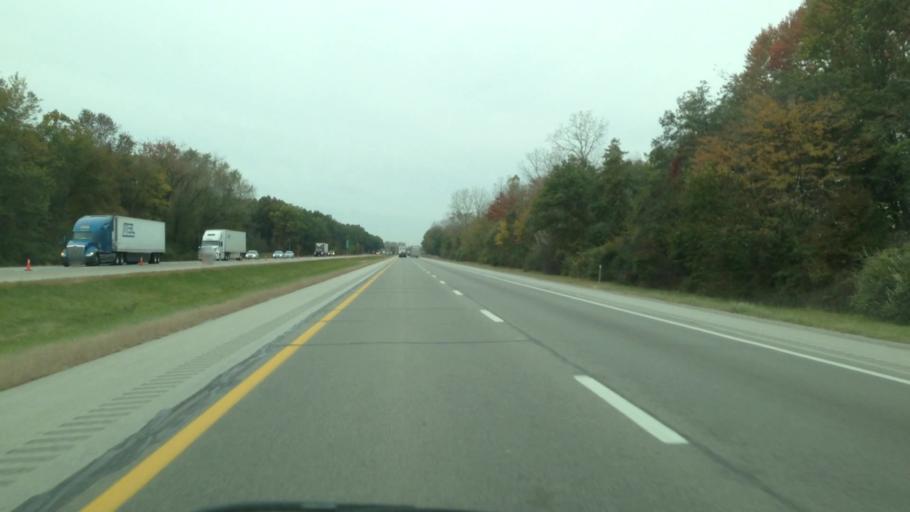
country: US
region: Ohio
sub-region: Lucas County
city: Holland
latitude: 41.5936
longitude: -83.7675
